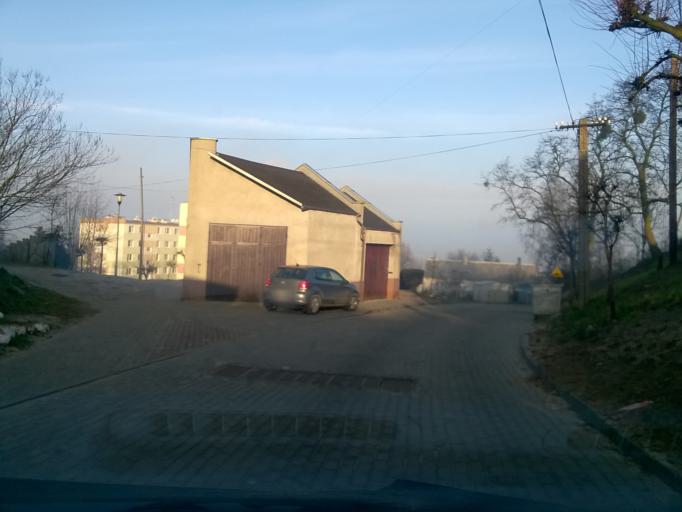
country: PL
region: Kujawsko-Pomorskie
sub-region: Powiat nakielski
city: Kcynia
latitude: 52.9925
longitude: 17.4862
